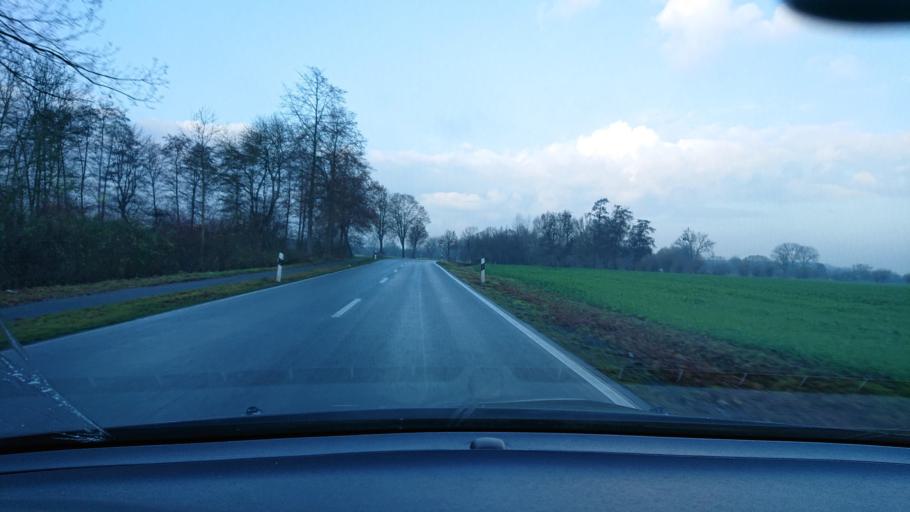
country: DE
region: North Rhine-Westphalia
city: Erwitte
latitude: 51.6171
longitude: 8.3222
